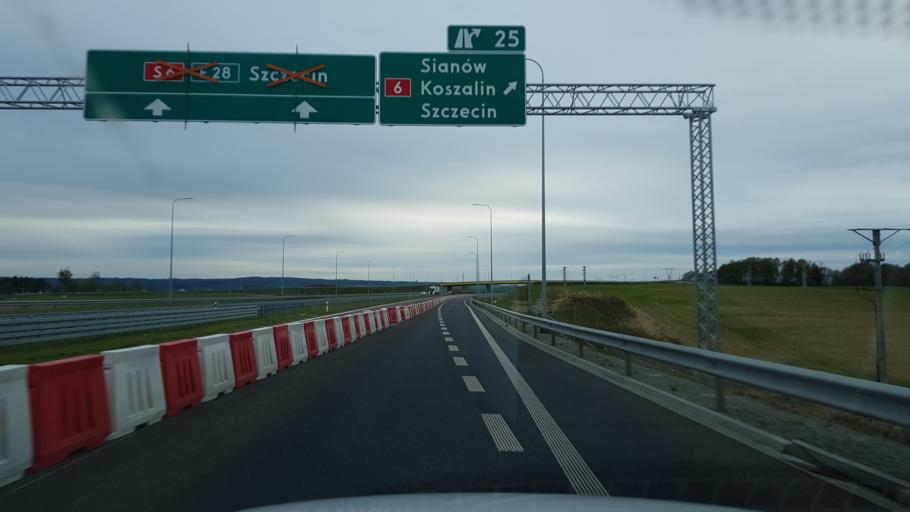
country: PL
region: West Pomeranian Voivodeship
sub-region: Powiat koszalinski
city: Sianow
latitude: 54.2412
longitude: 16.3303
